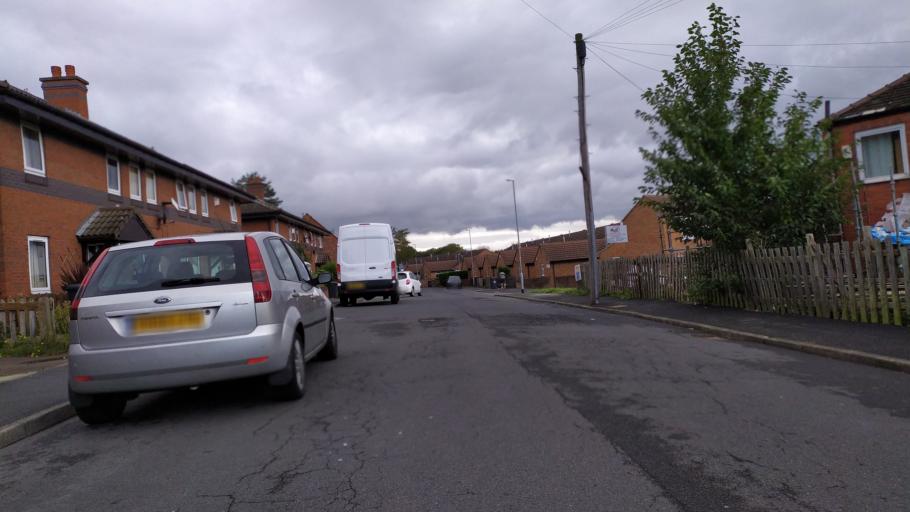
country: GB
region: England
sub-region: City and Borough of Leeds
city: Leeds
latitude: 53.8150
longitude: -1.5510
